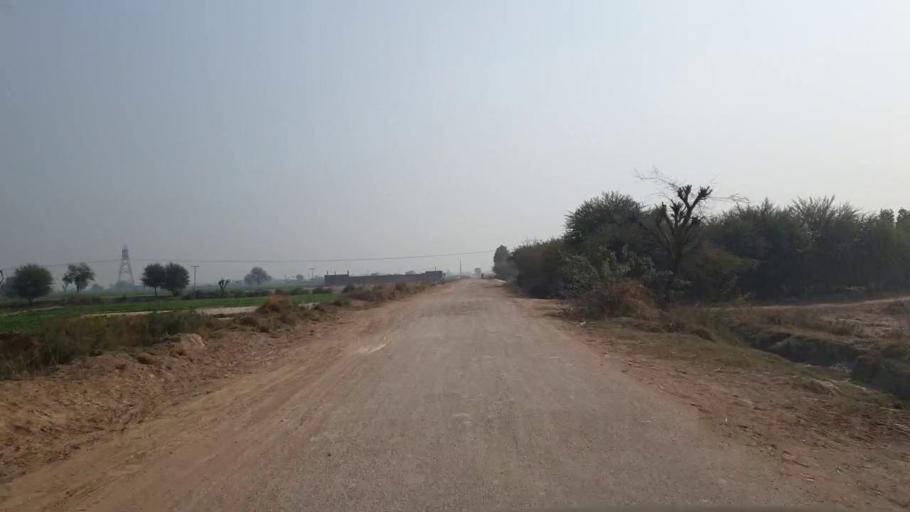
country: PK
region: Sindh
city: Hala
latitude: 25.9425
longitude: 68.4414
